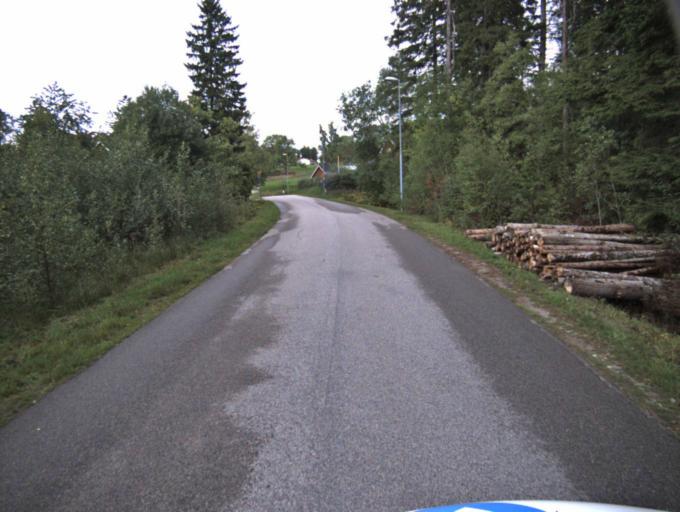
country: SE
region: Vaestra Goetaland
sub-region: Ulricehamns Kommun
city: Ulricehamn
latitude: 57.7869
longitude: 13.4408
